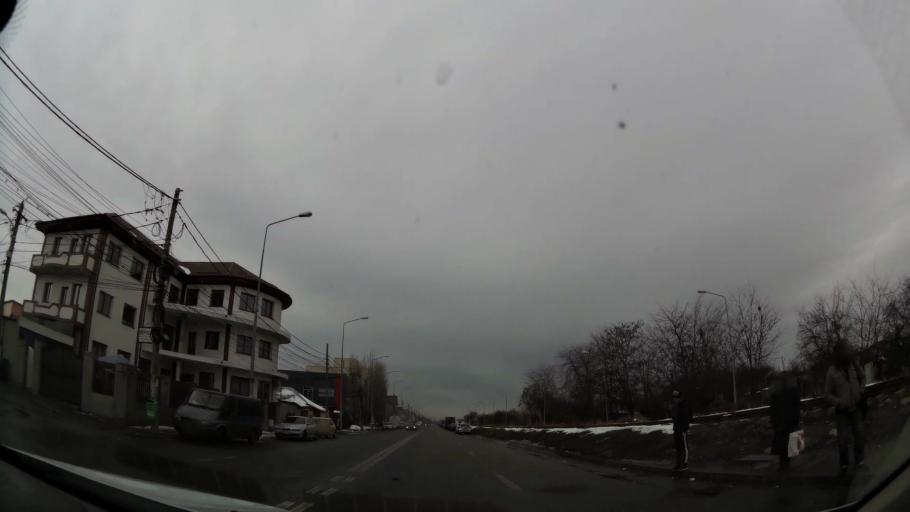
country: RO
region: Ilfov
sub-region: Comuna Pantelimon
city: Pantelimon
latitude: 44.4276
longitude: 26.2124
